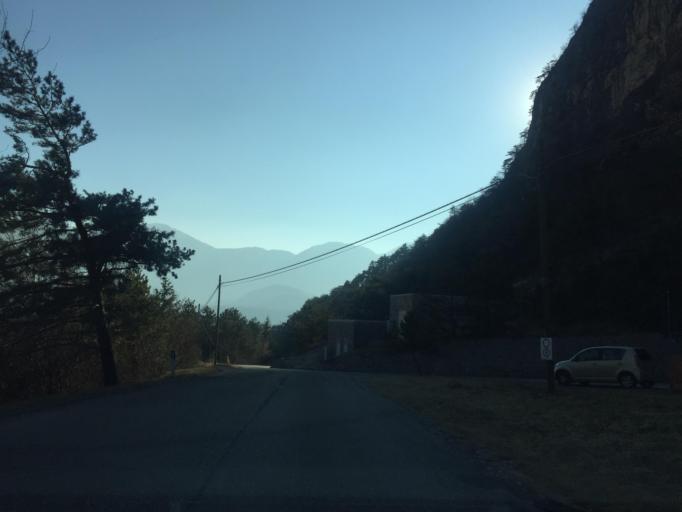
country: IT
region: Friuli Venezia Giulia
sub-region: Provincia di Udine
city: Tolmezzo
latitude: 46.4063
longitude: 13.0416
